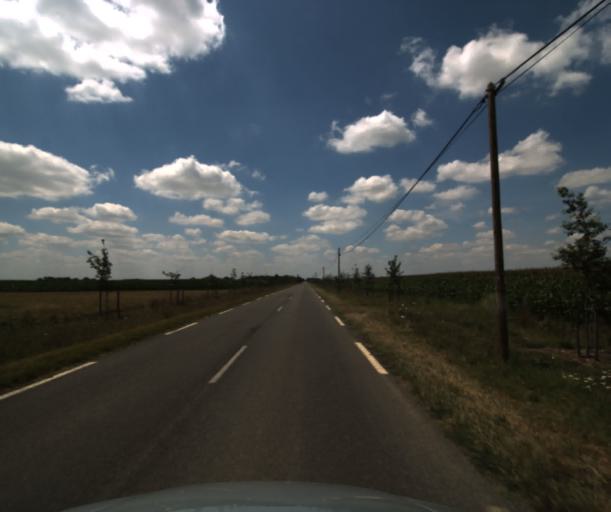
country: FR
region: Midi-Pyrenees
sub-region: Departement de la Haute-Garonne
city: Lherm
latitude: 43.4565
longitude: 1.2018
